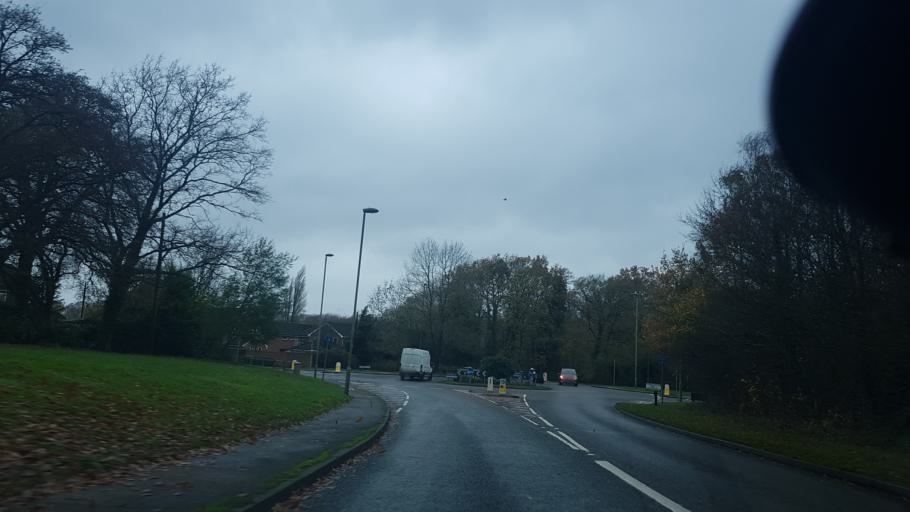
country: GB
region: England
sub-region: Surrey
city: Send
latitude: 51.2550
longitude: -0.5329
